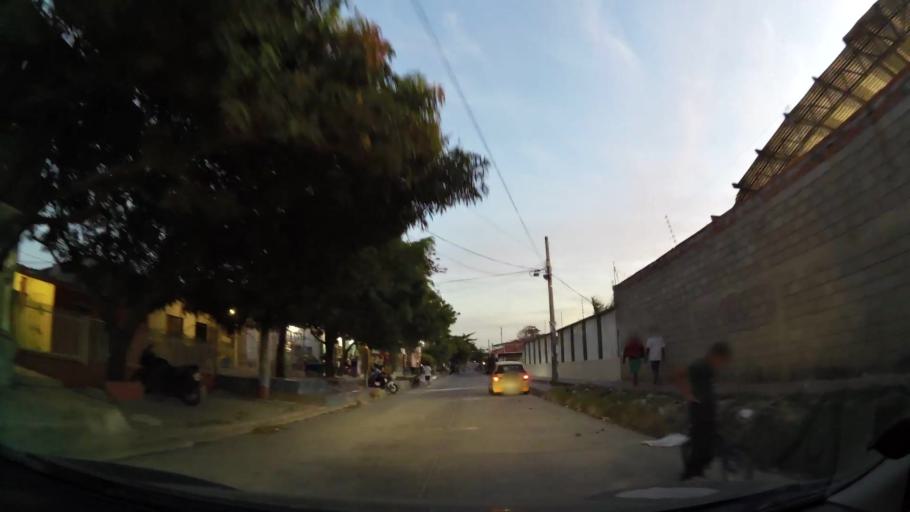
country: CO
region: Atlantico
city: Barranquilla
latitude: 10.9478
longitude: -74.8260
